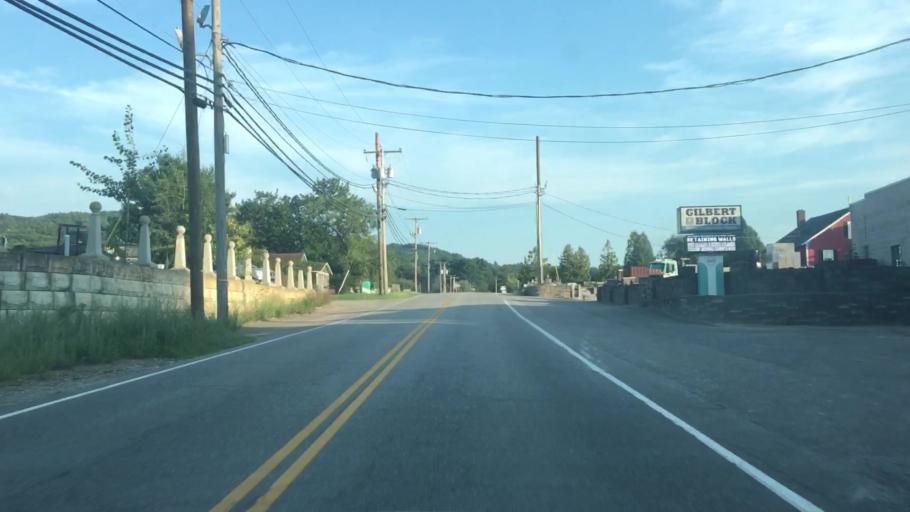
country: US
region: New Hampshire
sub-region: Belknap County
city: Laconia
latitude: 43.5118
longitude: -71.4530
